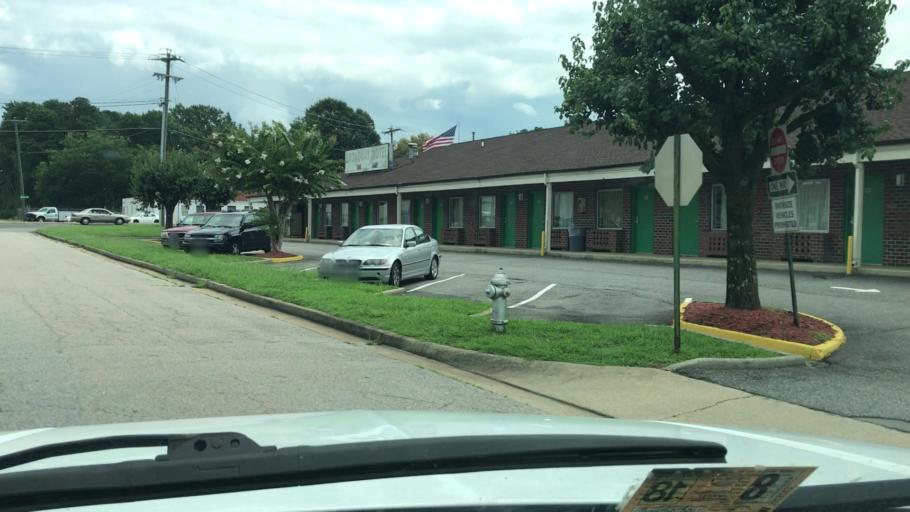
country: US
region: Virginia
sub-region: Henrico County
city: Chamberlayne
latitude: 37.6370
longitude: -77.4605
